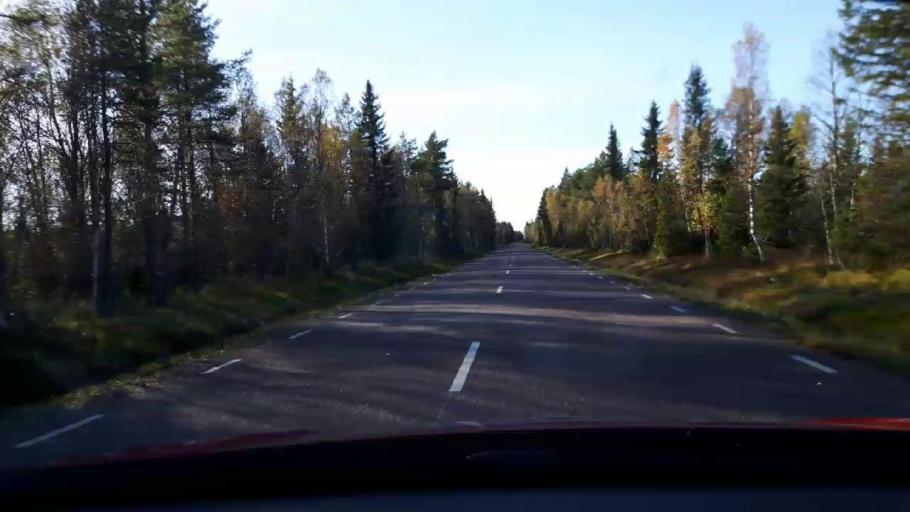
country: SE
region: Jaemtland
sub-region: Stroemsunds Kommun
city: Stroemsund
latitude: 63.8487
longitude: 15.2732
